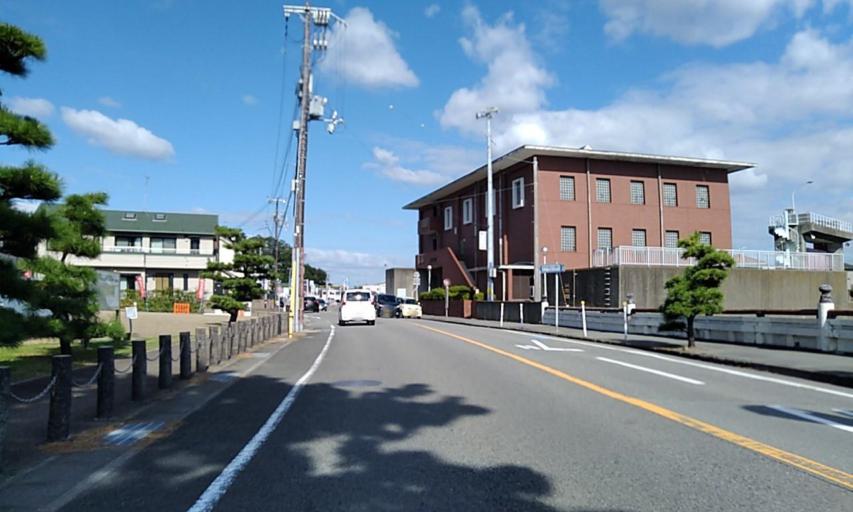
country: JP
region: Wakayama
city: Minato
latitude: 34.1875
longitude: 135.1733
